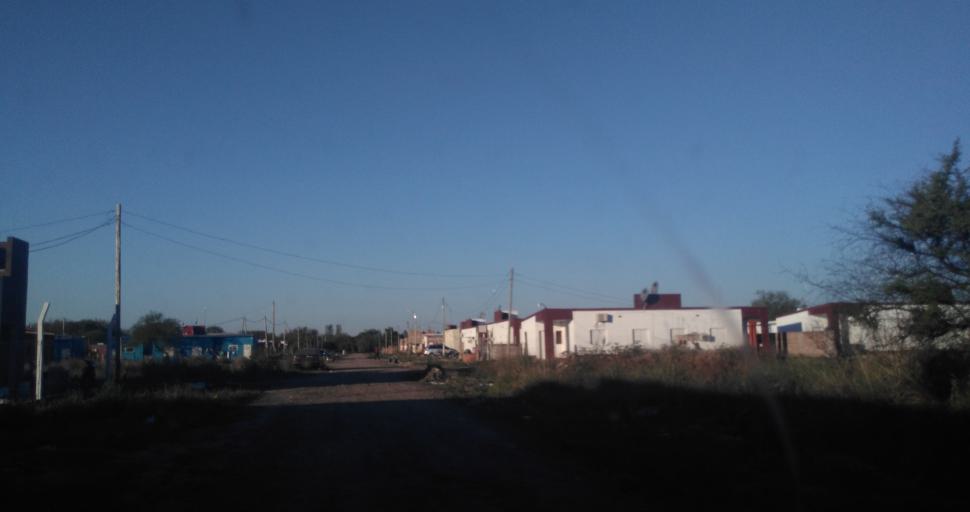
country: AR
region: Chaco
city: Resistencia
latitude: -27.4731
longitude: -59.0232
